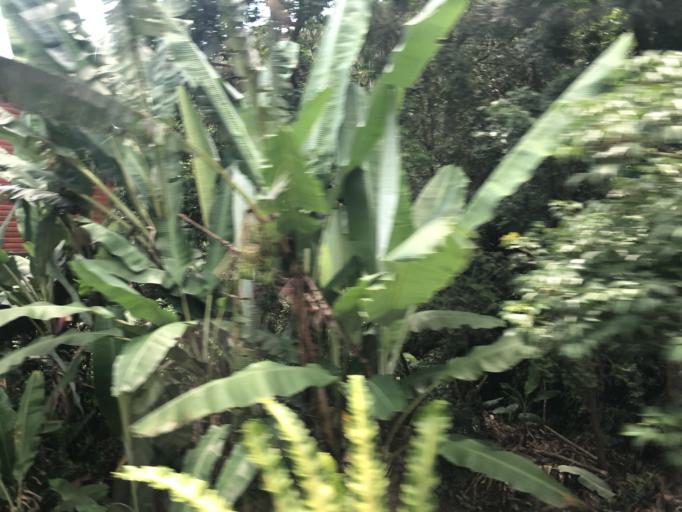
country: TW
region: Taipei
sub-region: Taipei
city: Banqiao
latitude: 24.9173
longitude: 121.4143
